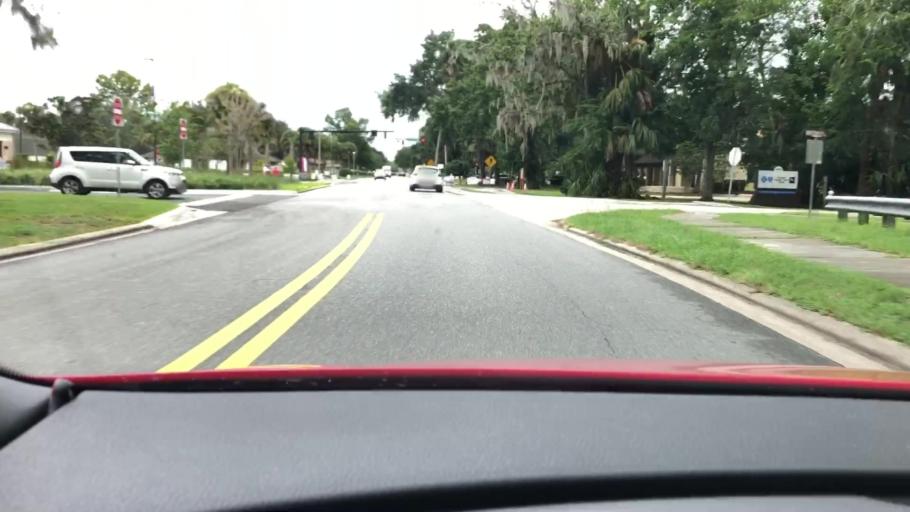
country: US
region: Florida
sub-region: Flagler County
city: Palm Coast
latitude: 29.5579
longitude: -81.2020
